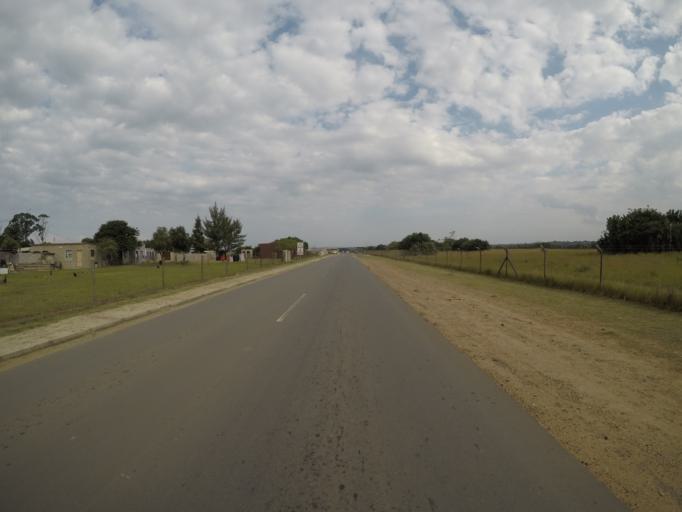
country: ZA
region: KwaZulu-Natal
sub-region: uThungulu District Municipality
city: Richards Bay
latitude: -28.7446
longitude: 32.0907
